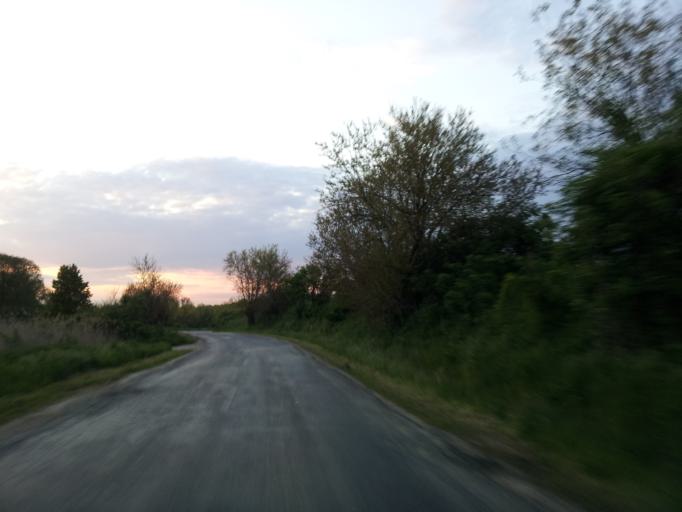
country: HU
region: Pest
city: Perbal
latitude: 47.6332
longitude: 18.7571
